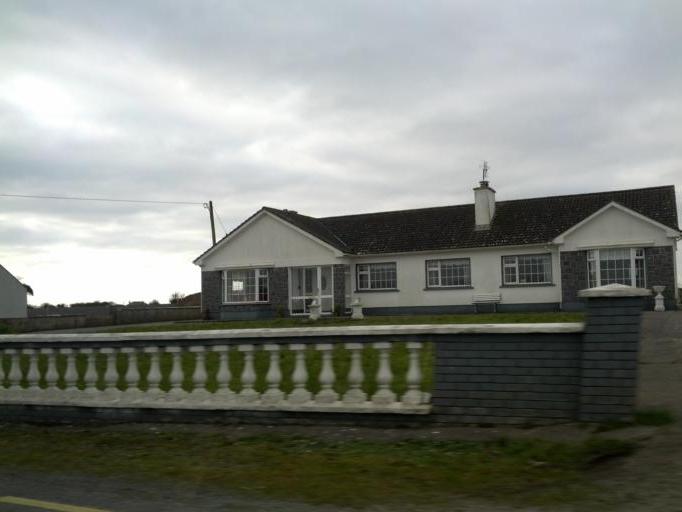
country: IE
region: Connaught
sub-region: County Galway
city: Athenry
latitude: 53.2229
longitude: -8.8052
